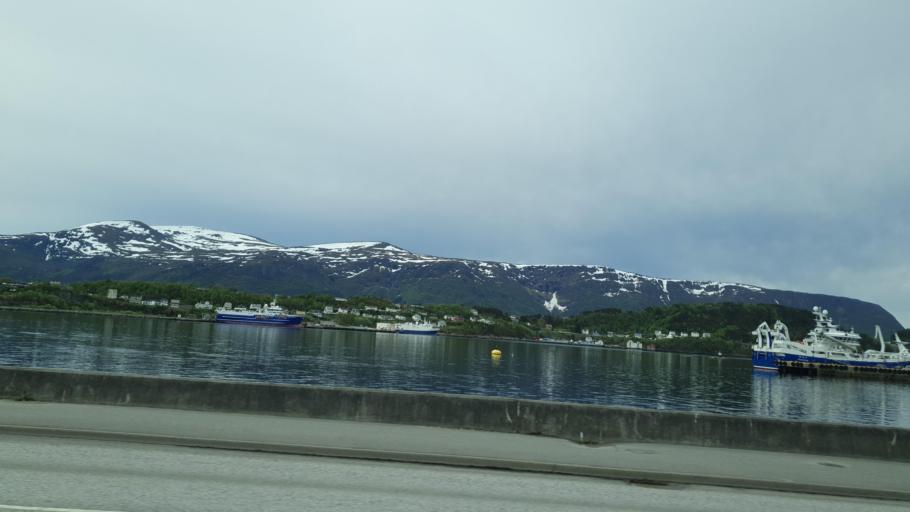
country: NO
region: More og Romsdal
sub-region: Alesund
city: Alesund
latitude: 62.4708
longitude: 6.1614
